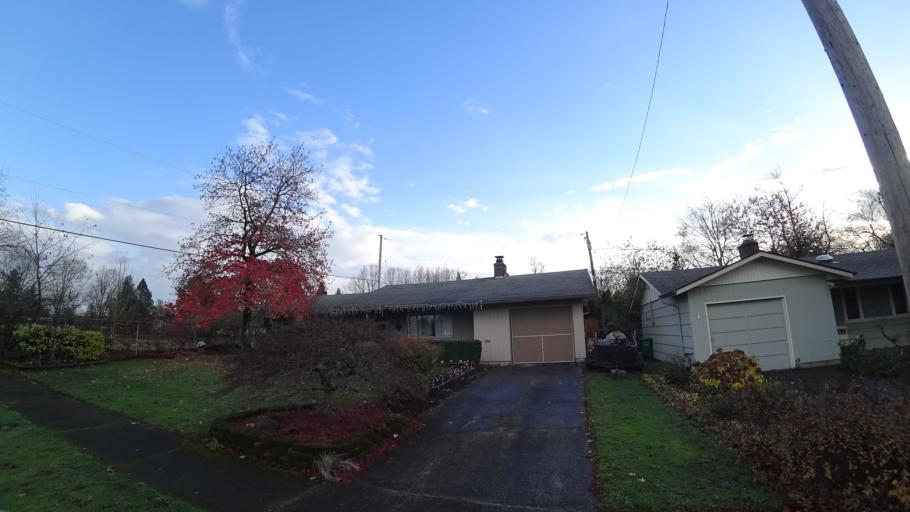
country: US
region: Oregon
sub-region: Multnomah County
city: Lents
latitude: 45.5203
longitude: -122.5451
